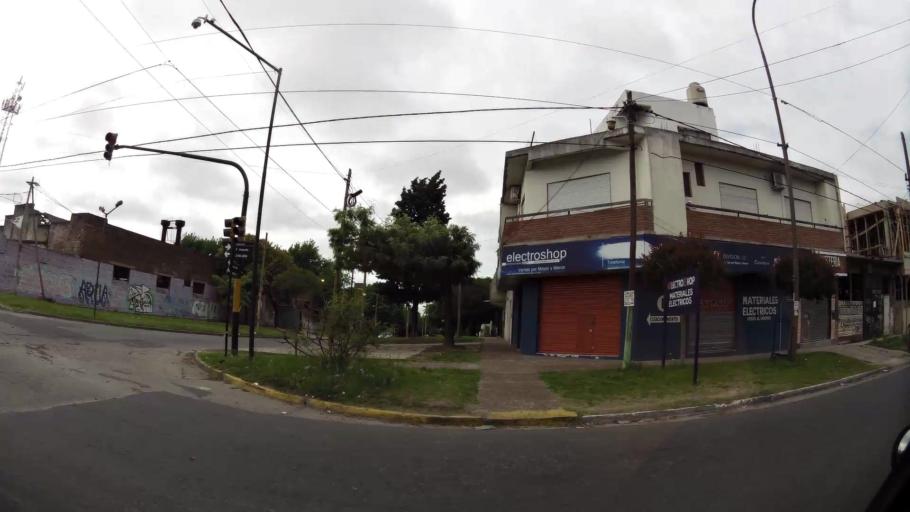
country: AR
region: Buenos Aires
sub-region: Partido de Quilmes
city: Quilmes
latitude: -34.7439
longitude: -58.2836
